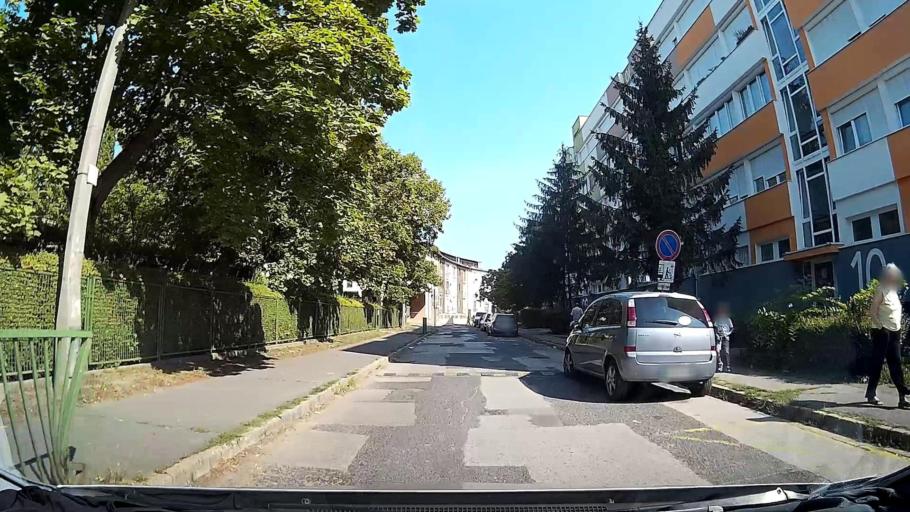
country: HU
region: Pest
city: Szentendre
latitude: 47.6681
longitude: 19.0614
